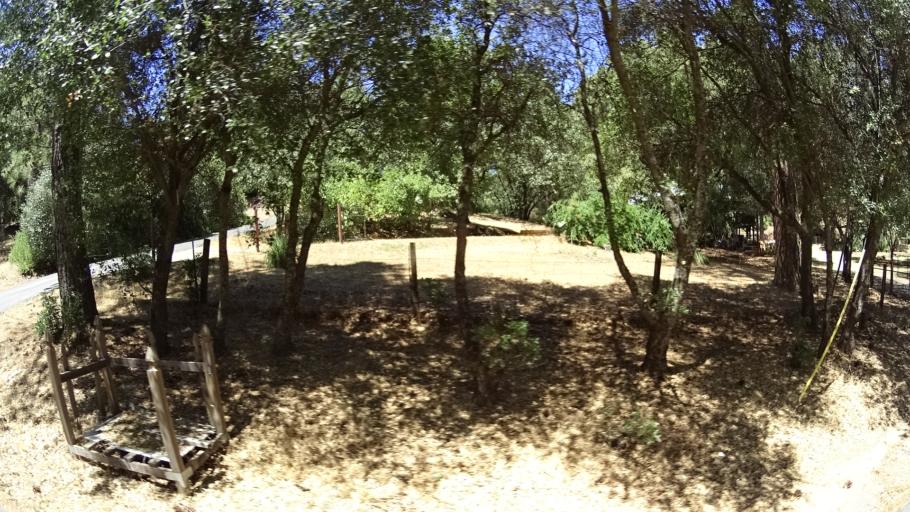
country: US
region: California
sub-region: Calaveras County
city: Murphys
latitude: 38.1397
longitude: -120.4849
